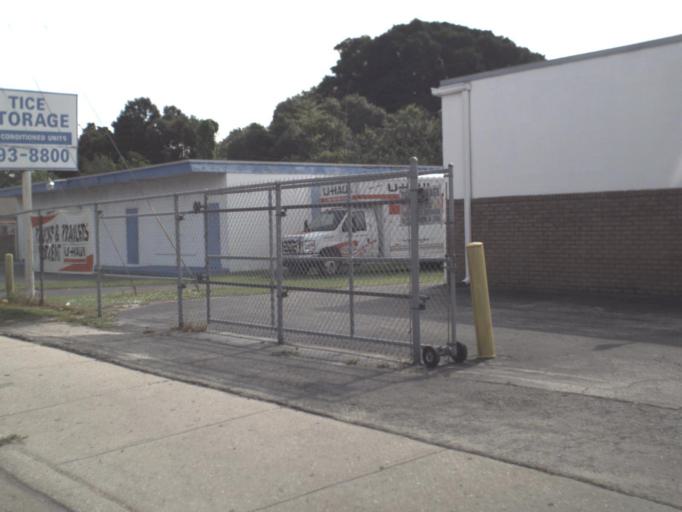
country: US
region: Florida
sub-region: Lee County
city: Tice
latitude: 26.6712
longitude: -81.8215
